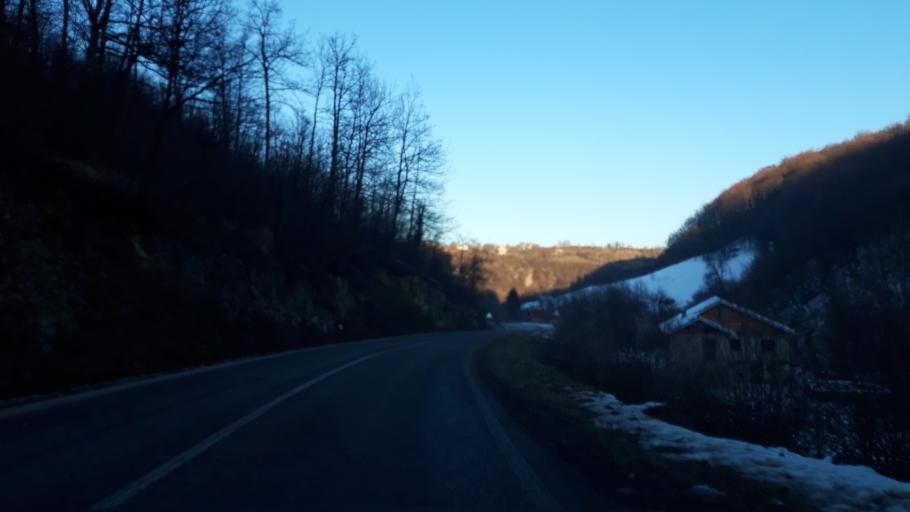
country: BA
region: Republika Srpska
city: Vlasenica
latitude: 44.1816
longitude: 18.9651
